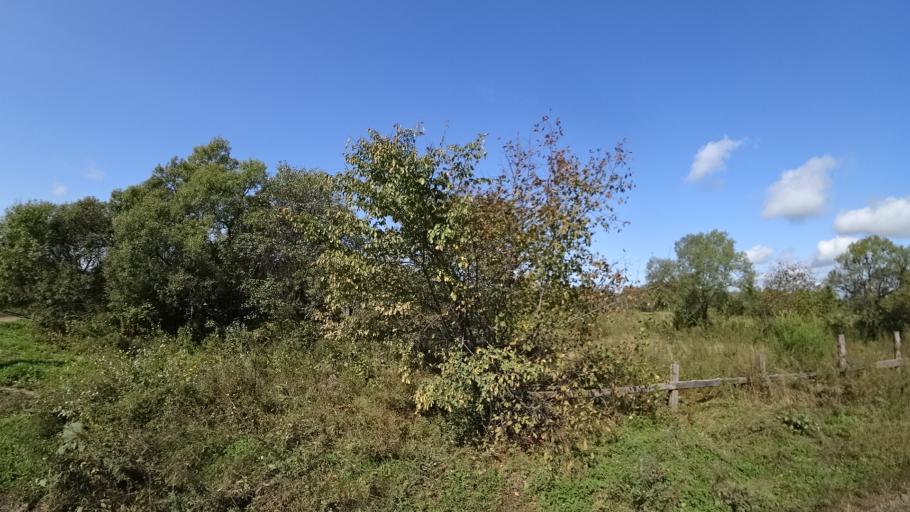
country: RU
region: Amur
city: Arkhara
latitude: 49.4065
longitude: 130.1575
